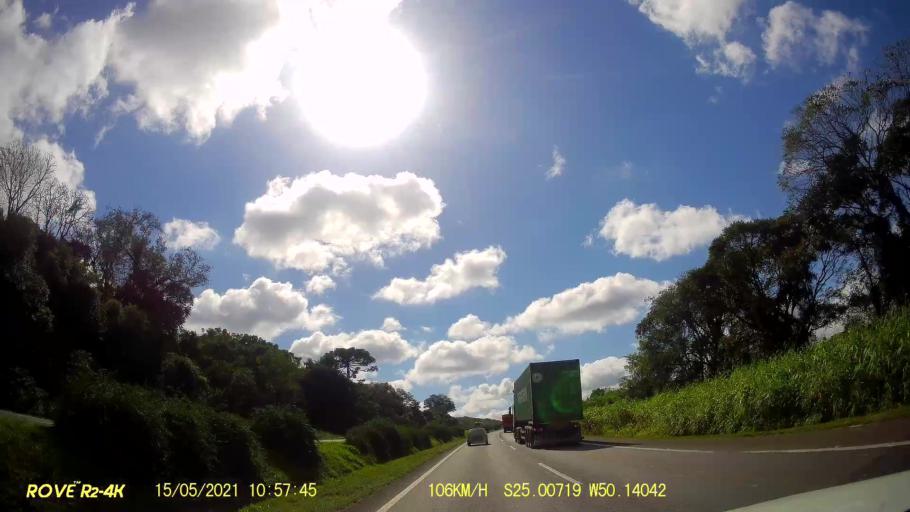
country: BR
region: Parana
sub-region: Carambei
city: Carambei
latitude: -25.0066
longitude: -50.1401
